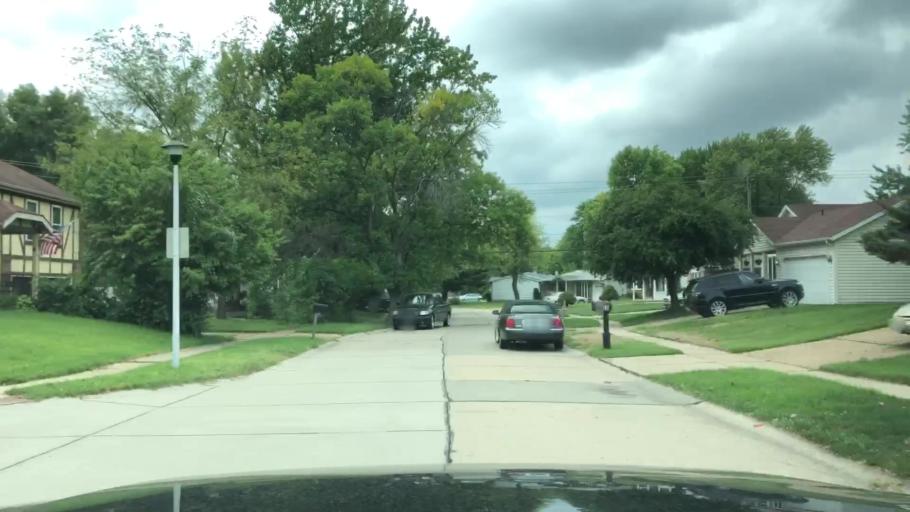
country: US
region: Missouri
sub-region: Saint Louis County
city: Florissant
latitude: 38.8097
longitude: -90.3106
